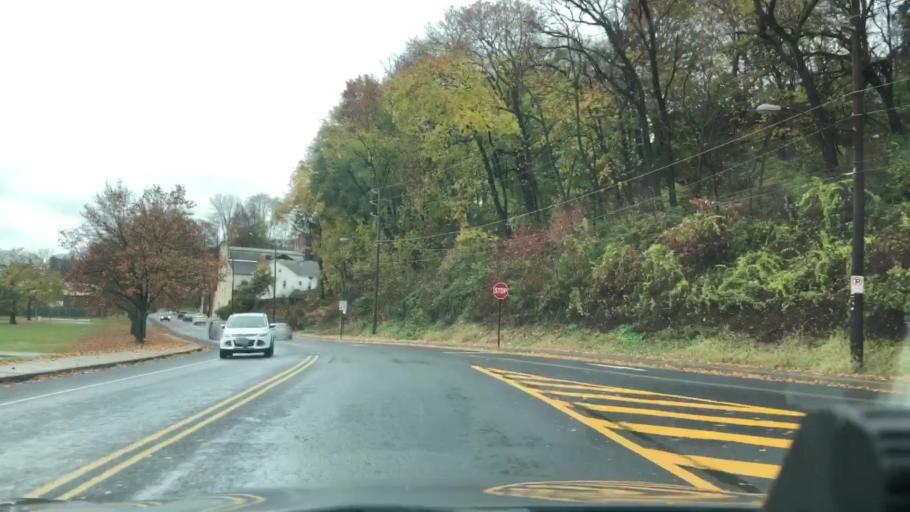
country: US
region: Pennsylvania
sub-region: Lehigh County
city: Allentown
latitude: 40.5971
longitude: -75.4785
